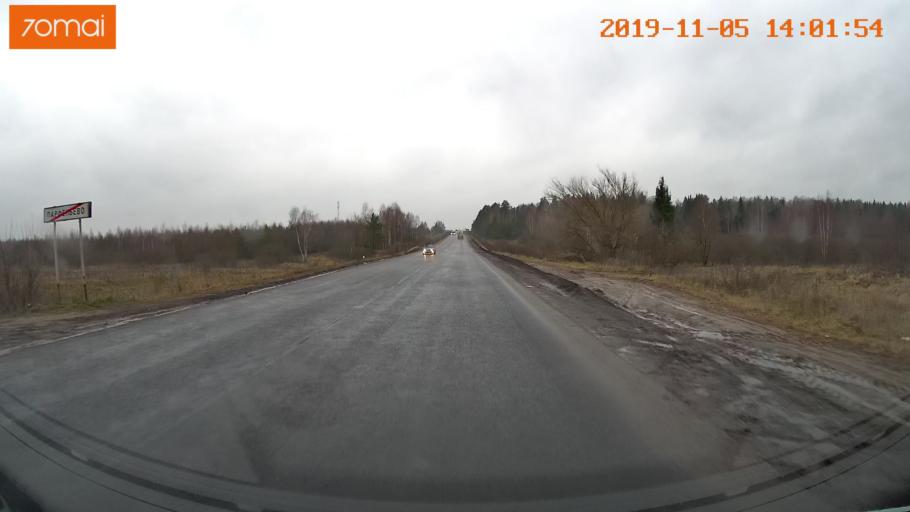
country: RU
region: Ivanovo
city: Kokhma
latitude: 57.0060
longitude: 41.2231
